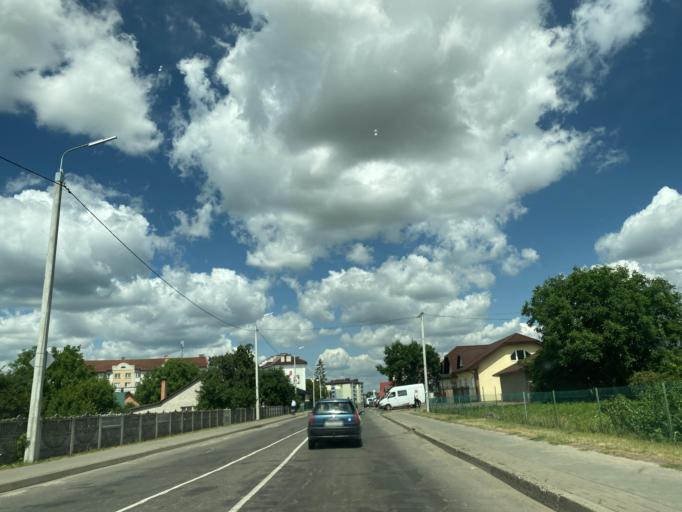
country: BY
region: Brest
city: Ivanava
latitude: 52.1456
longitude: 25.5421
